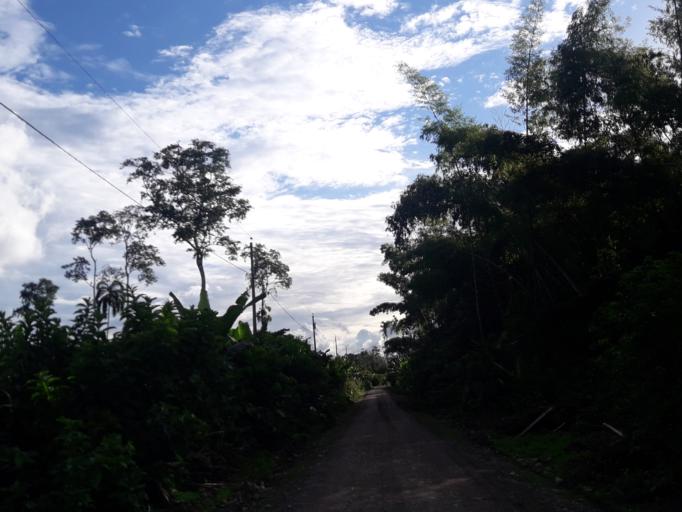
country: EC
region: Orellana
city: Boca Suno
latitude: -0.8832
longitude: -77.2899
